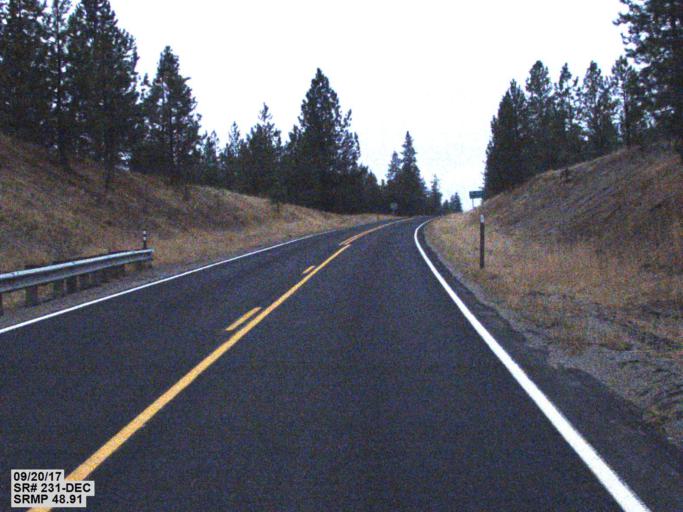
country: US
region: Washington
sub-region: Spokane County
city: Fairchild Air Force Base
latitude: 47.8925
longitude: -117.8270
